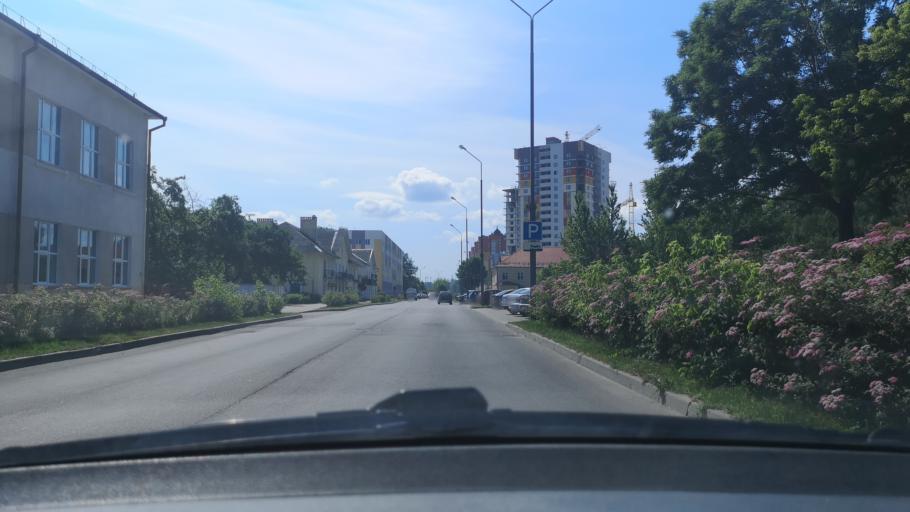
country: BY
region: Brest
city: Brest
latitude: 52.0987
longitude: 23.7019
